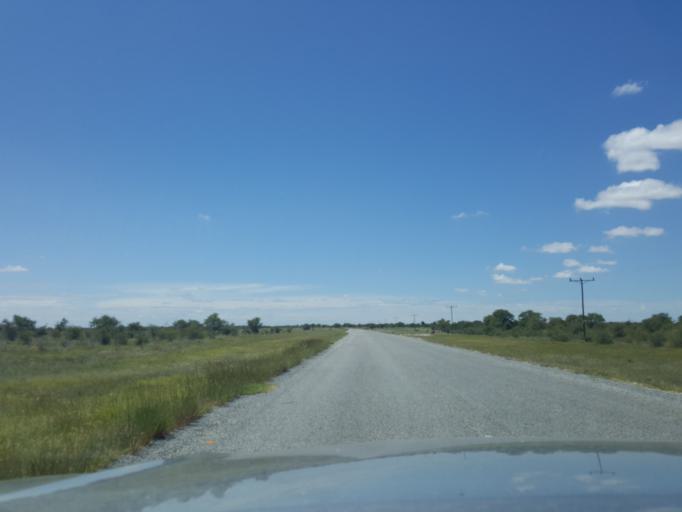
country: BW
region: Central
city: Nata
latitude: -20.1579
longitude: 25.8395
